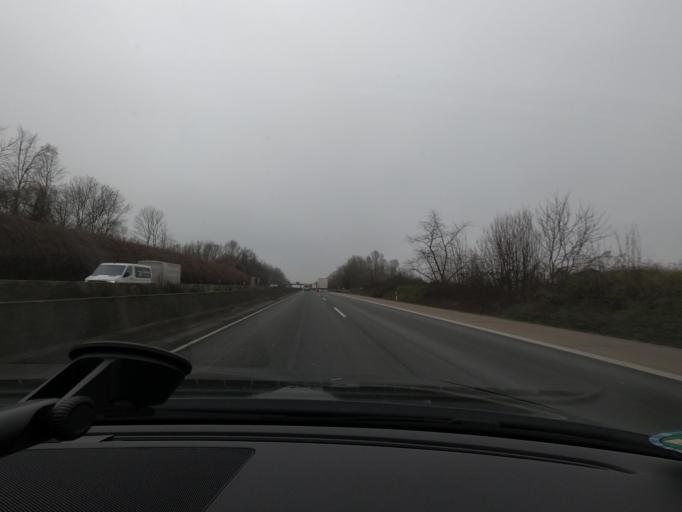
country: DE
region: North Rhine-Westphalia
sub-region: Regierungsbezirk Koln
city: Kerpen
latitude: 50.9137
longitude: 6.6837
